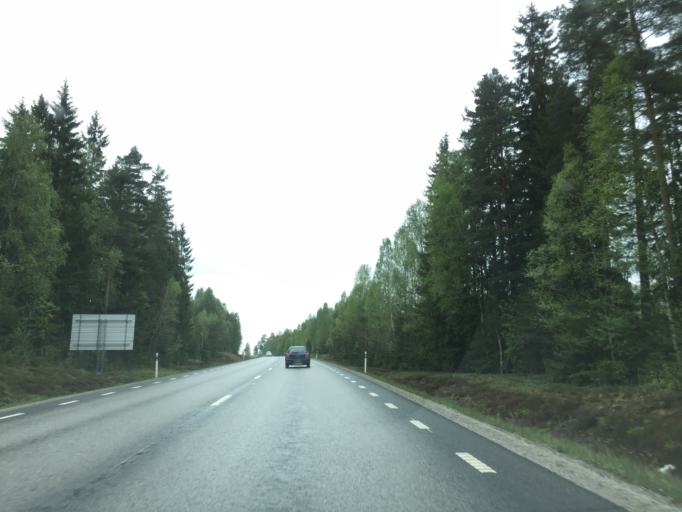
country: SE
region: OErebro
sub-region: Lindesbergs Kommun
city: Lindesberg
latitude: 59.5576
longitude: 15.2207
